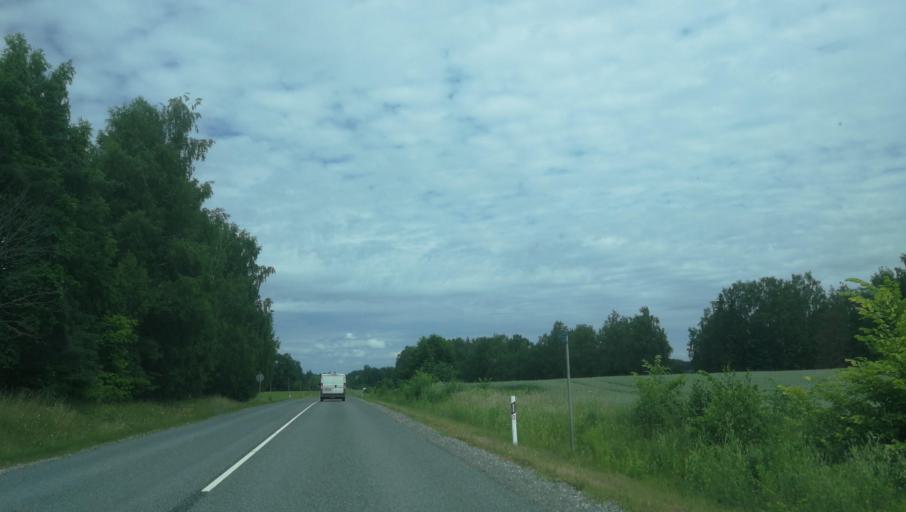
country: LV
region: Naukseni
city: Naukseni
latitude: 57.7351
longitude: 25.4255
